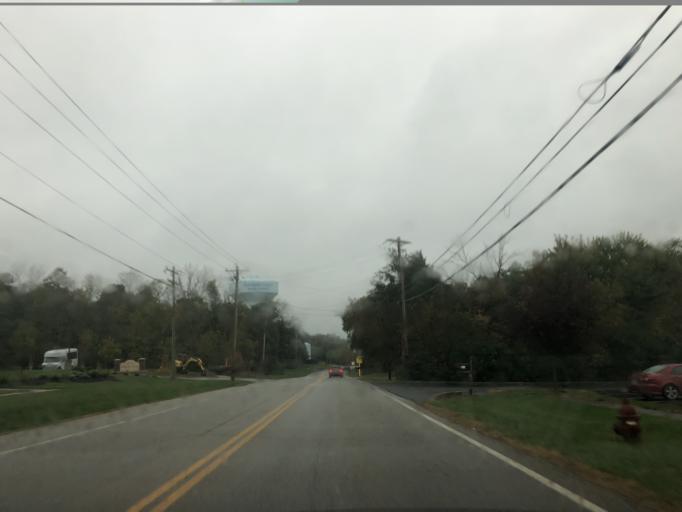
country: US
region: Ohio
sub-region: Clermont County
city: Mulberry
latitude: 39.2281
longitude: -84.2586
